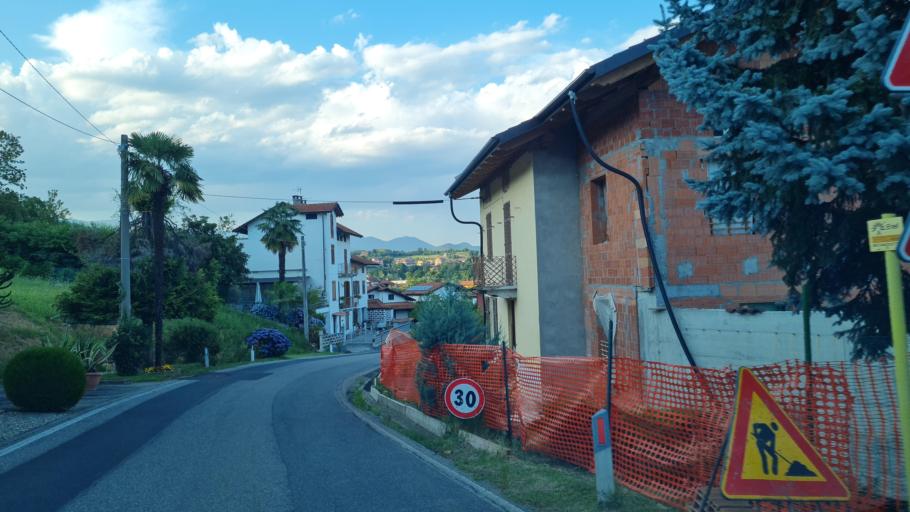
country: IT
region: Piedmont
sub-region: Provincia di Biella
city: Camburzano
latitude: 45.5485
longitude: 8.0056
